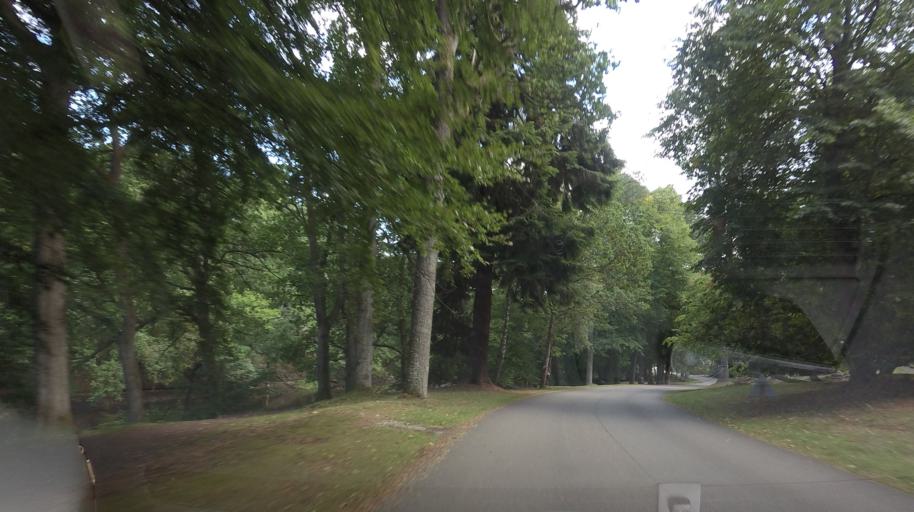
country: GB
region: Scotland
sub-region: Aberdeenshire
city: Banchory
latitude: 57.0588
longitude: -2.4280
